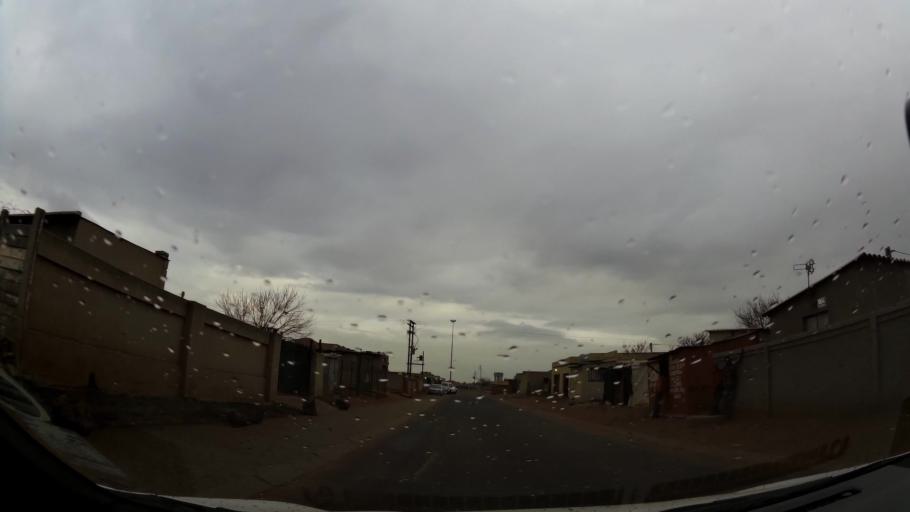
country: ZA
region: Gauteng
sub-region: Ekurhuleni Metropolitan Municipality
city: Germiston
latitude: -26.3786
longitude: 28.1801
